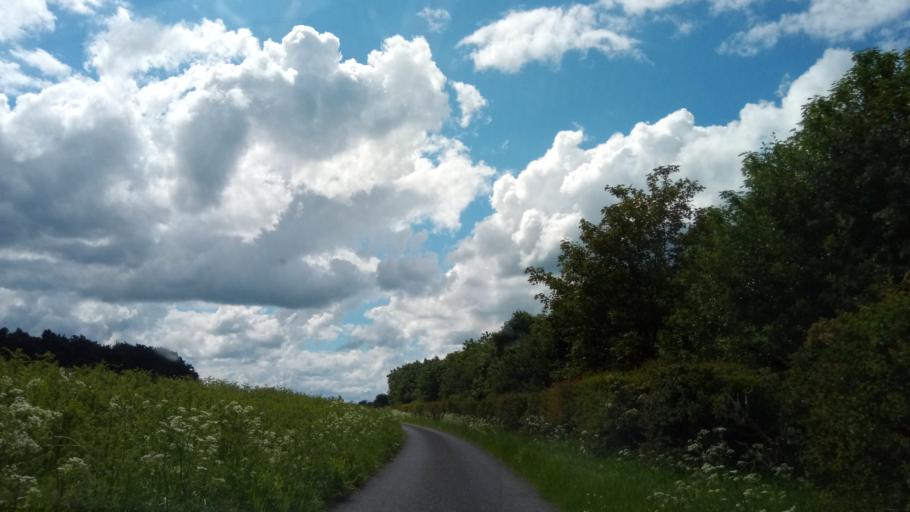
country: GB
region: Scotland
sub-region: The Scottish Borders
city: Coldstream
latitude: 55.5998
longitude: -2.2748
